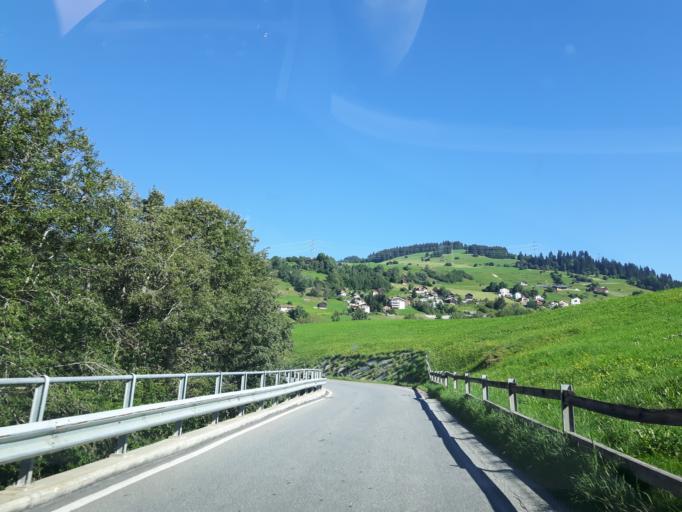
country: CH
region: Grisons
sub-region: Surselva District
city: Breil
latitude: 46.7756
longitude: 9.1091
